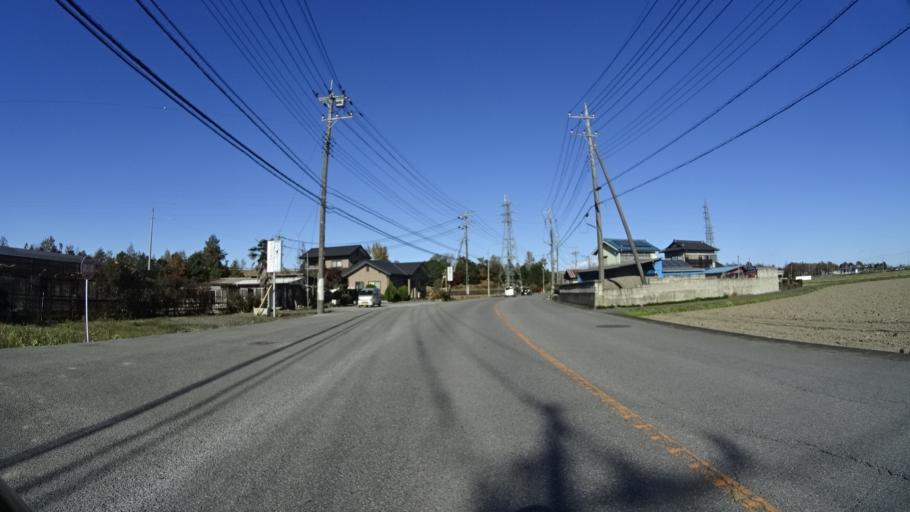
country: JP
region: Tochigi
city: Mibu
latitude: 36.4364
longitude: 139.7502
